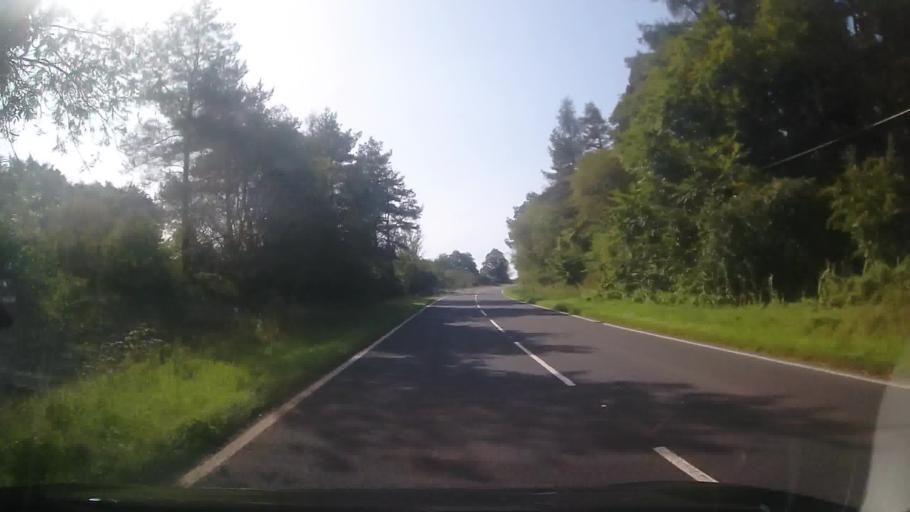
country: GB
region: Wales
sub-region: Sir Powys
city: Rhayader
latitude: 52.1234
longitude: -3.6164
